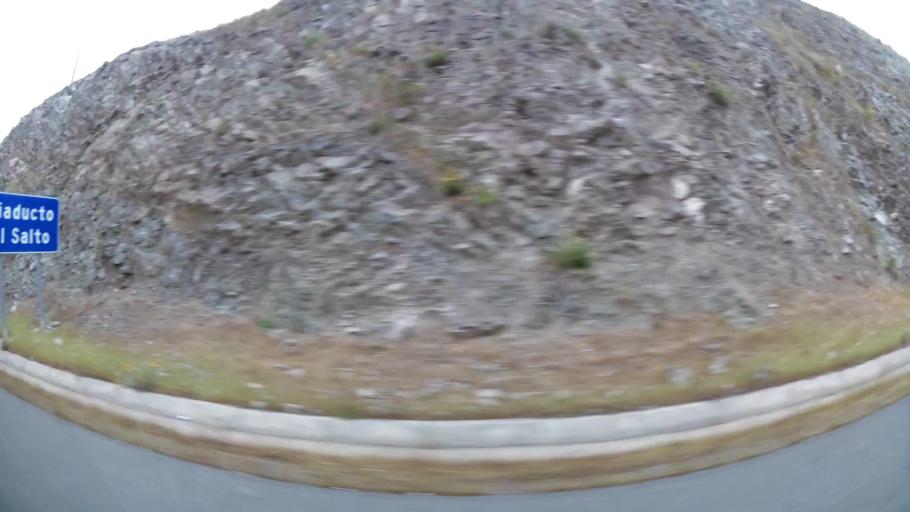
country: CL
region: Santiago Metropolitan
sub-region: Provincia de Santiago
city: Villa Presidente Frei, Nunoa, Santiago, Chile
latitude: -33.3852
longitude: -70.6026
